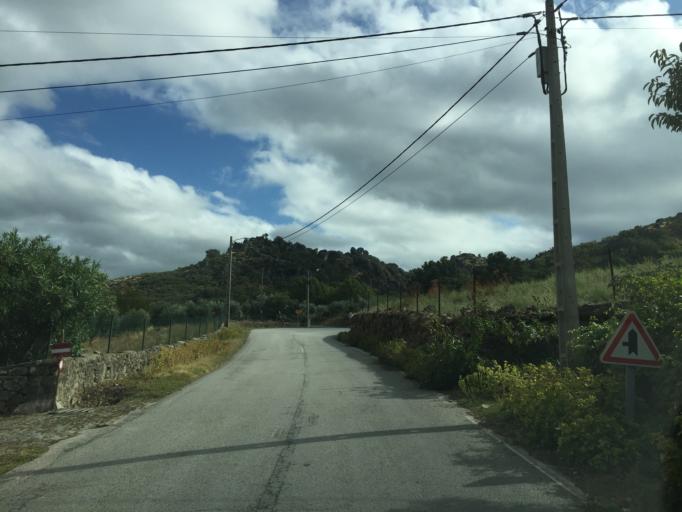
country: PT
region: Portalegre
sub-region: Marvao
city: Marvao
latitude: 39.4002
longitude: -7.3702
